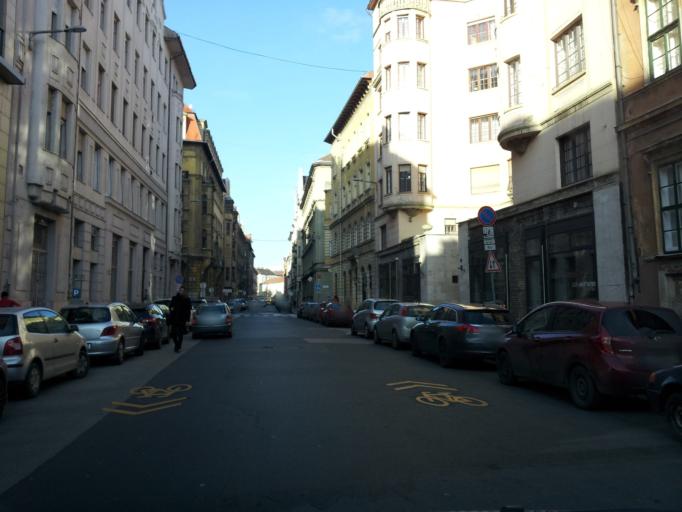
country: HU
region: Budapest
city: Budapest IX. keruelet
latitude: 47.4852
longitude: 19.0623
